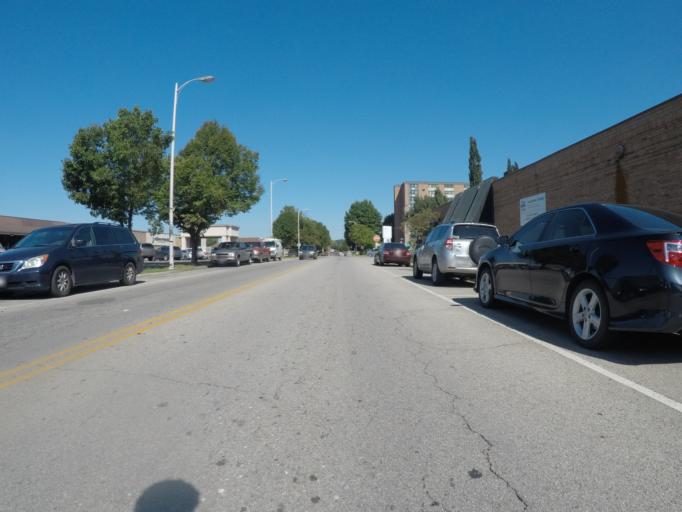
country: US
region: Ohio
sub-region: Lawrence County
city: Ironton
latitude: 38.5355
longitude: -82.6866
